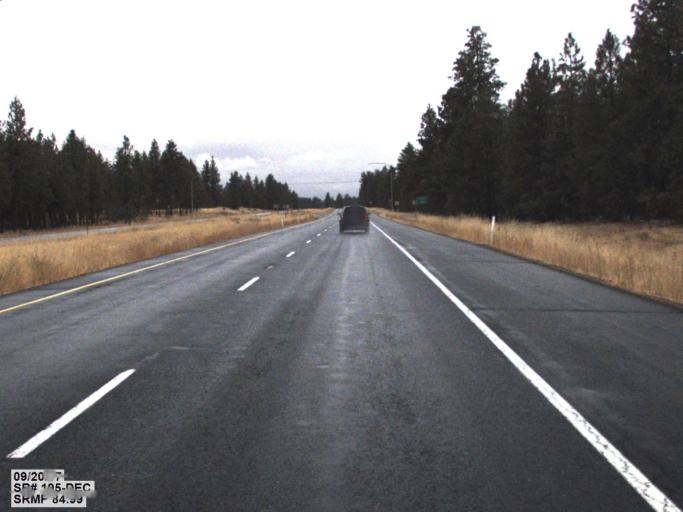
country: US
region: Washington
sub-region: Spokane County
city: Spokane
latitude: 47.5020
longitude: -117.4008
